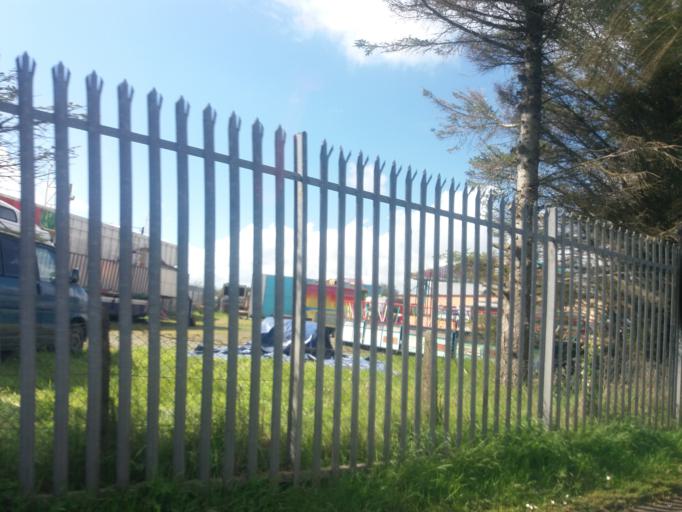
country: IE
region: Leinster
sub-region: Loch Garman
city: Castlebridge
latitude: 52.3889
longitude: -6.3666
